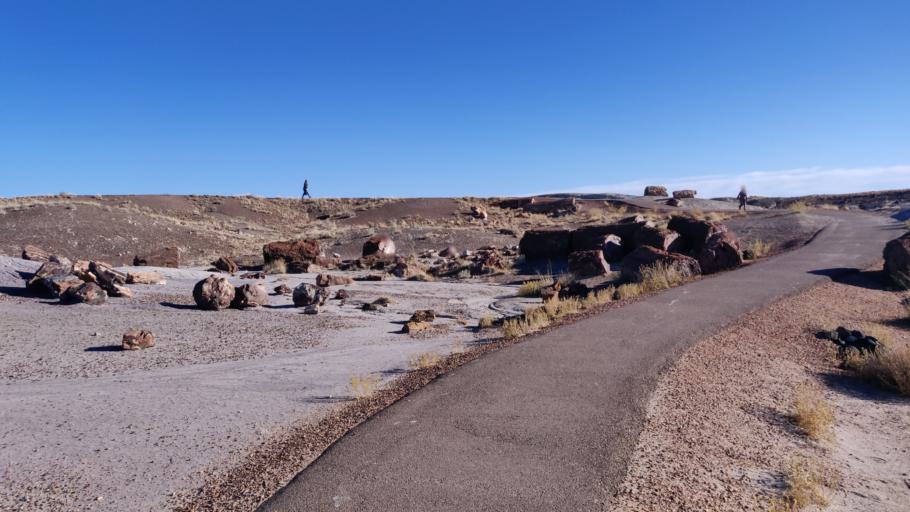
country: US
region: Arizona
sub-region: Navajo County
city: Holbrook
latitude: 34.8642
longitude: -109.7905
